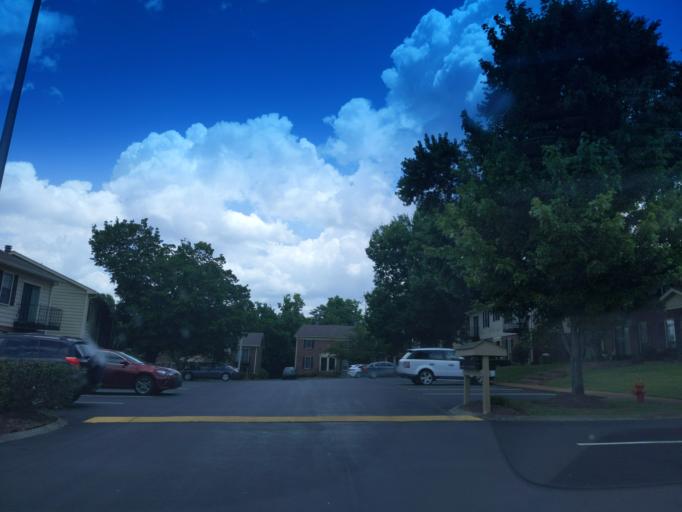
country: US
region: Tennessee
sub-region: Williamson County
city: Brentwood
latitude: 36.0387
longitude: -86.7758
